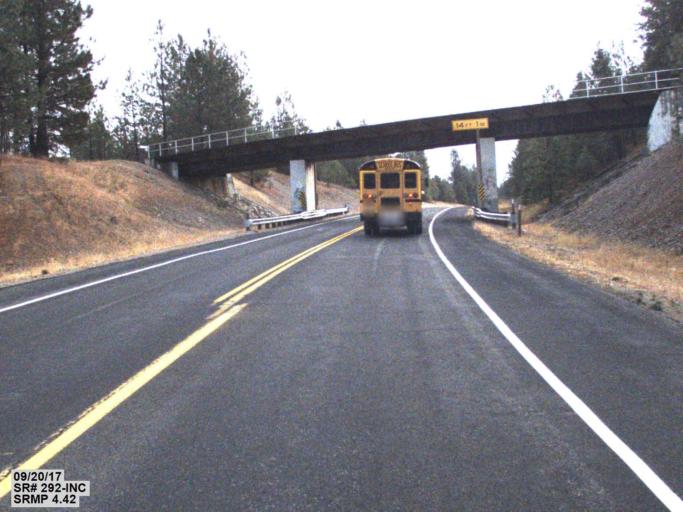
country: US
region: Washington
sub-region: Spokane County
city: Deer Park
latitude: 48.0651
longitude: -117.6508
